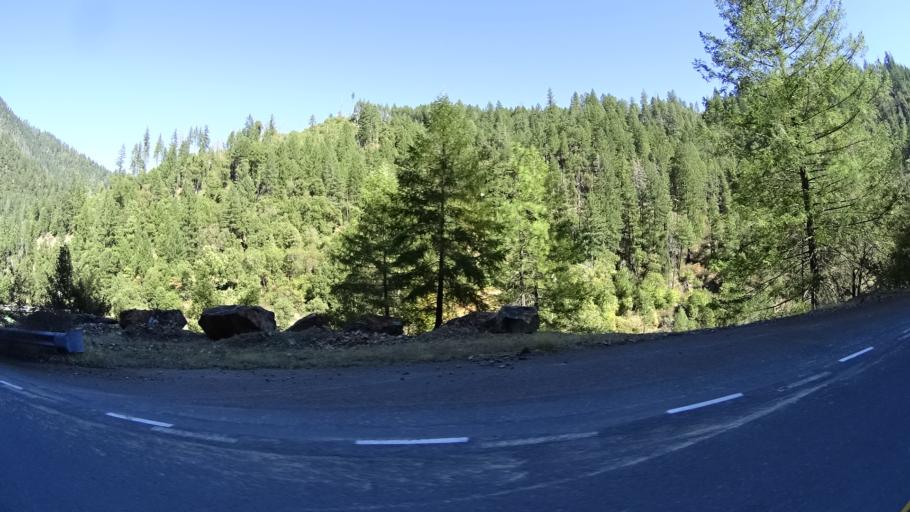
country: US
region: California
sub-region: Siskiyou County
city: Happy Camp
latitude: 41.3745
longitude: -123.4203
